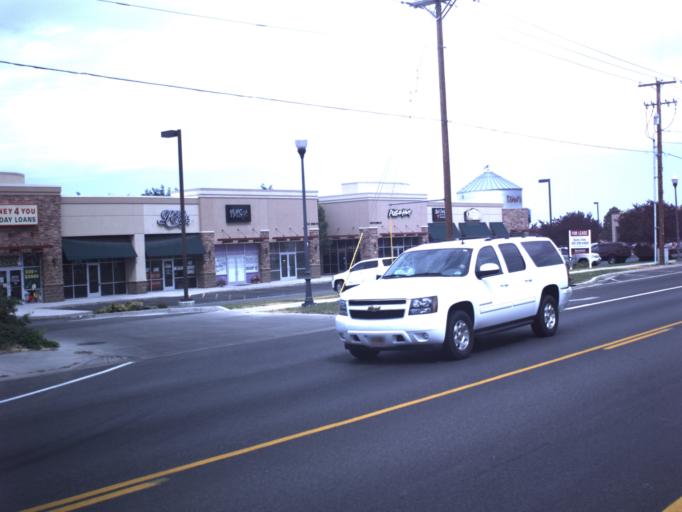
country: US
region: Utah
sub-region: Davis County
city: Clinton
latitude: 41.1448
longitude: -112.0644
